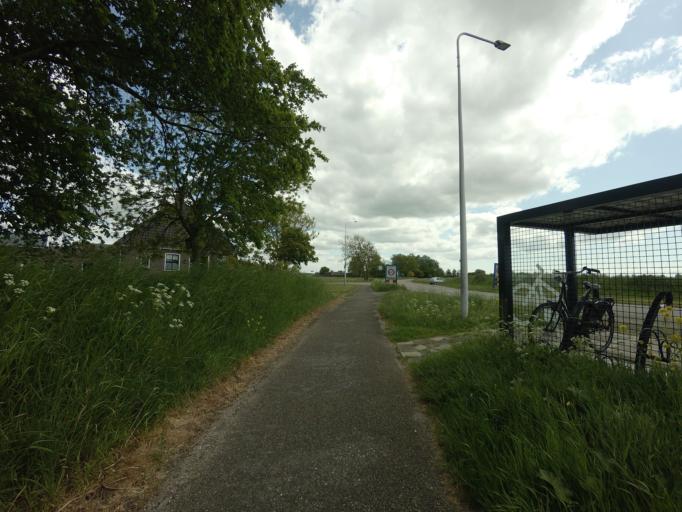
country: NL
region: Friesland
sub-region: Sudwest Fryslan
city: Bolsward
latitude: 53.0929
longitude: 5.5349
